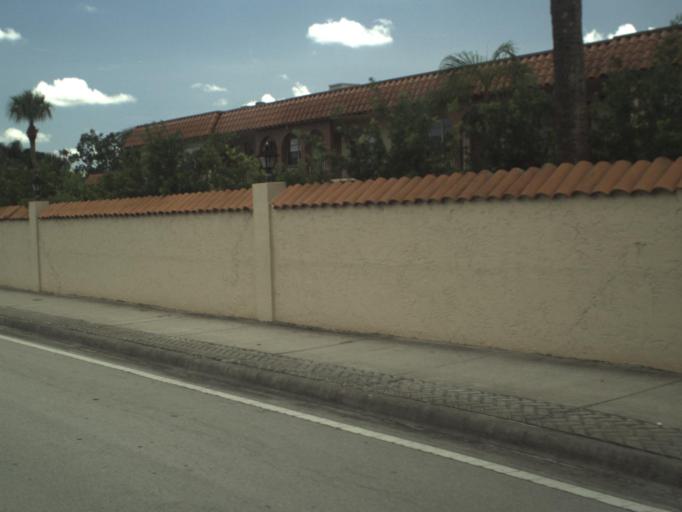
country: US
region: Florida
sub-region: Martin County
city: Palm City
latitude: 27.1736
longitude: -80.2528
